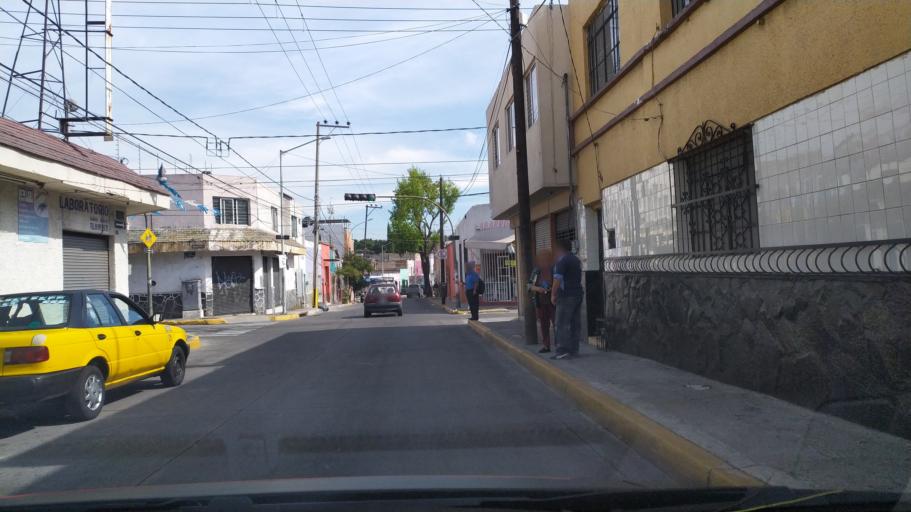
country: MX
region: Jalisco
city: Tlaquepaque
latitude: 20.6821
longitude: -103.3332
